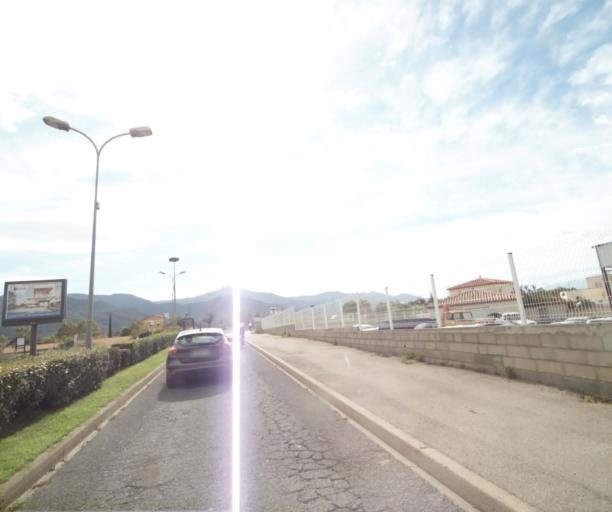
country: FR
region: Languedoc-Roussillon
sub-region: Departement des Pyrenees-Orientales
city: Argelers
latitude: 42.5521
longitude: 3.0105
